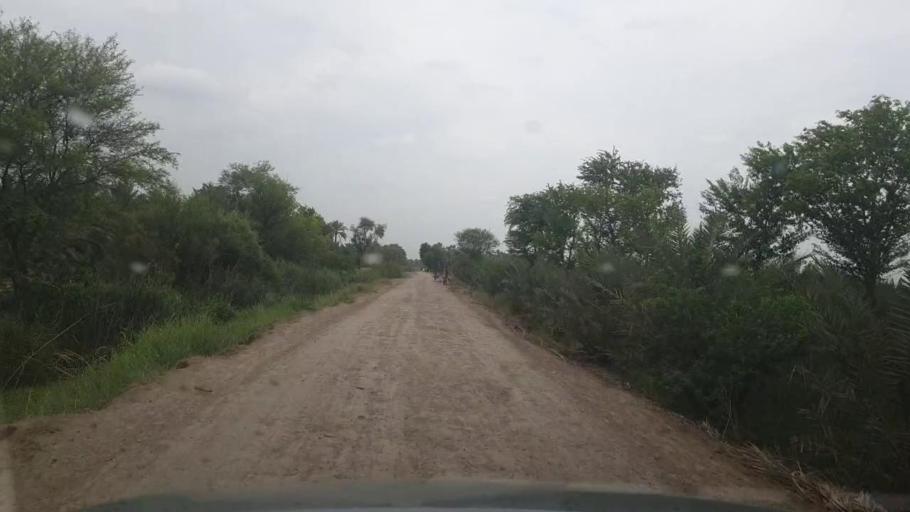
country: PK
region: Sindh
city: Khairpur
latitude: 27.5570
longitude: 68.7009
